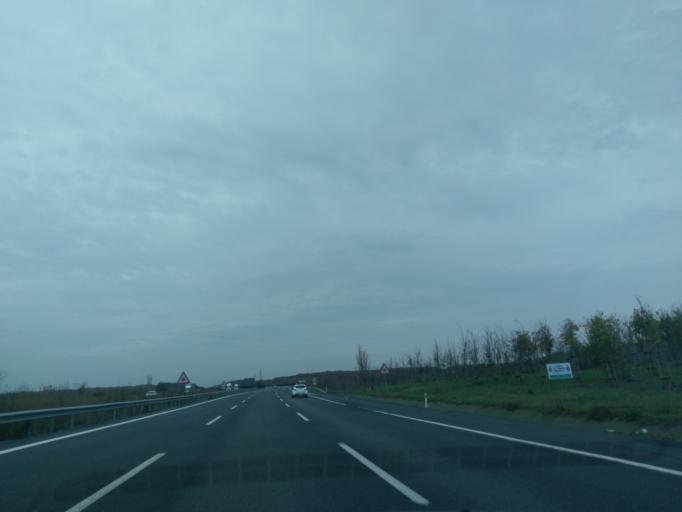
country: TR
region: Istanbul
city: Canta
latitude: 41.1767
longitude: 28.1158
